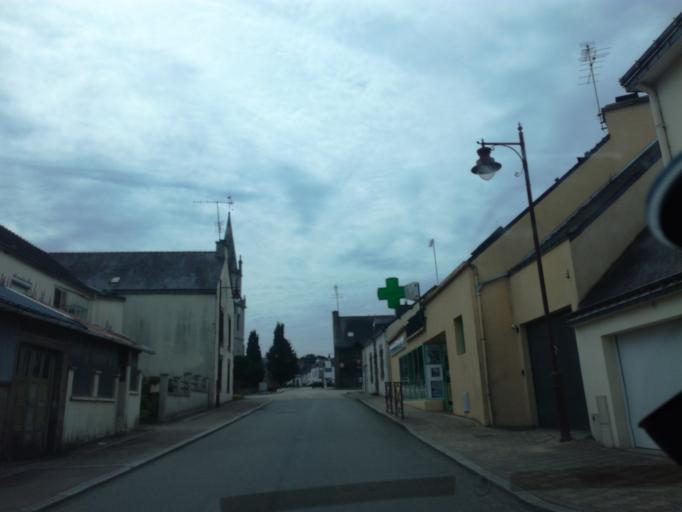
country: FR
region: Brittany
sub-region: Departement du Morbihan
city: Saint-Thuriau
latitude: 48.0172
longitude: -2.9507
